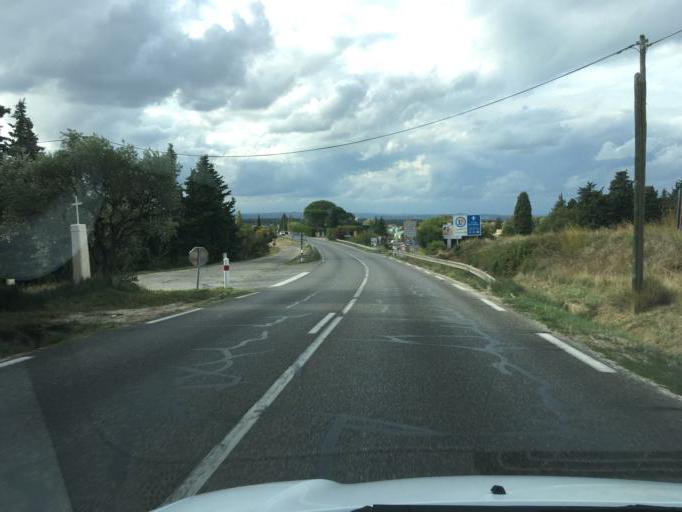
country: FR
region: Provence-Alpes-Cote d'Azur
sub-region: Departement du Vaucluse
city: Morieres-les-Avignon
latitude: 43.9373
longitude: 4.9154
